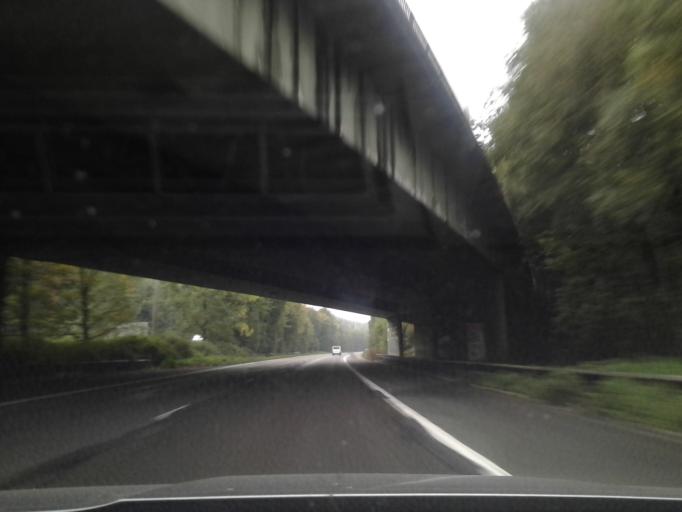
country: BE
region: Wallonia
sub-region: Province du Hainaut
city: La Louviere
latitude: 50.5036
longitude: 4.1625
